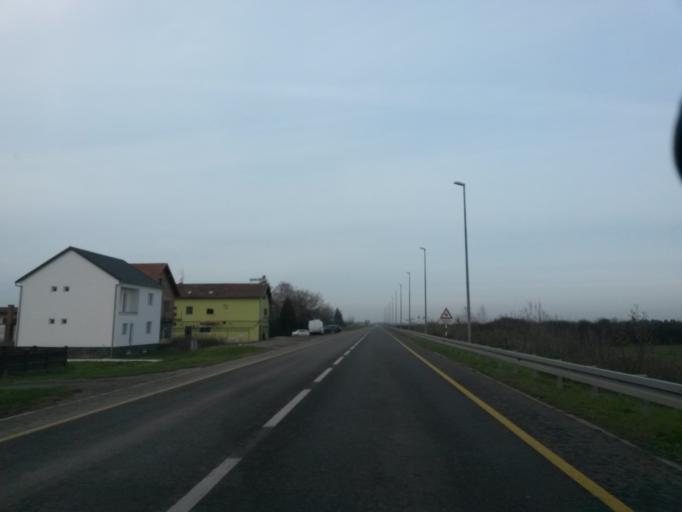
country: HR
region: Vukovarsko-Srijemska
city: Brsadin
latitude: 45.3910
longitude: 18.9256
